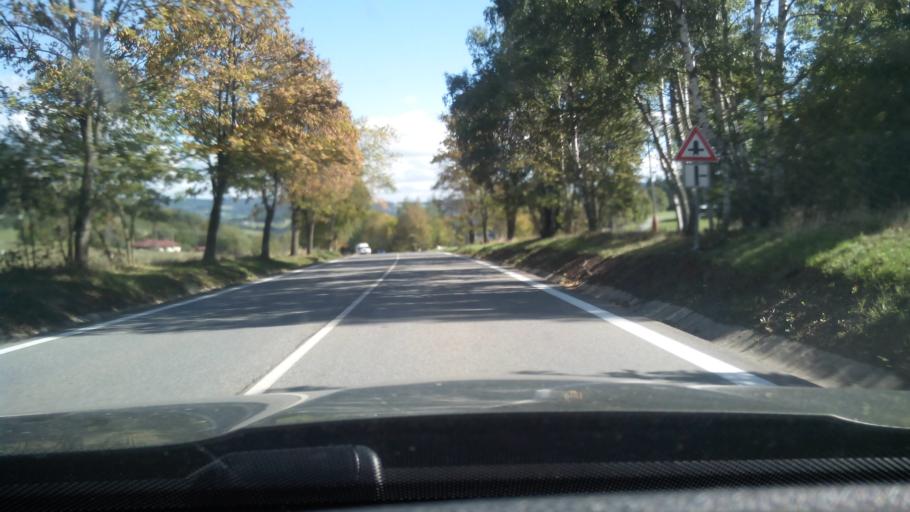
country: CZ
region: Jihocesky
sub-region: Okres Prachatice
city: Vimperk
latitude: 49.0610
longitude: 13.7591
